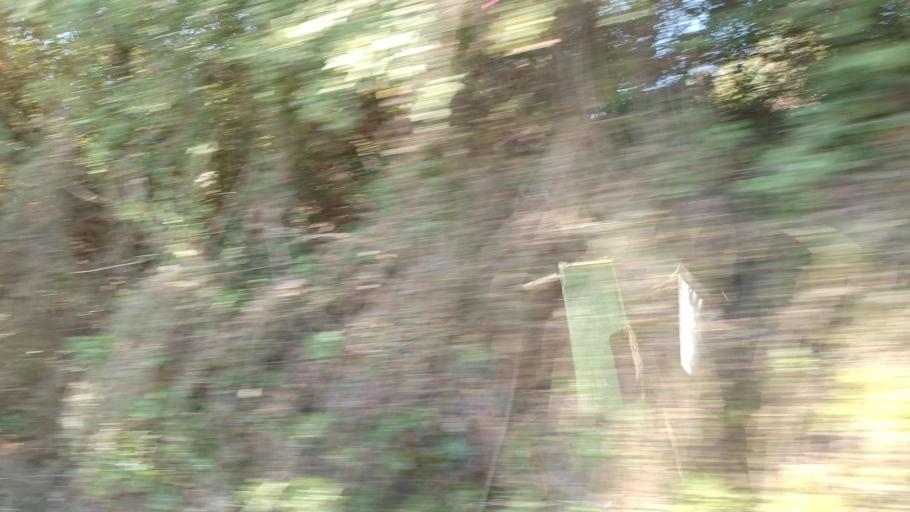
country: CY
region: Pafos
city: Polis
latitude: 34.9723
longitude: 32.4230
